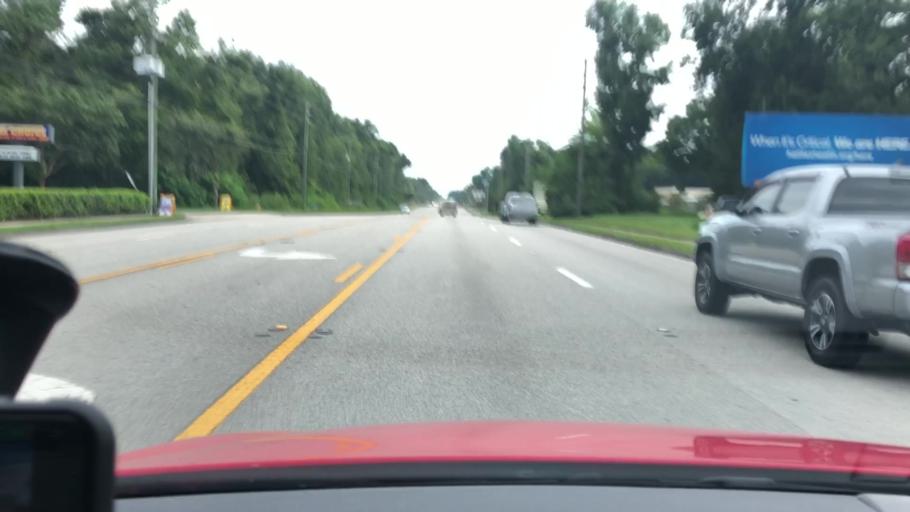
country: US
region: Florida
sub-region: Volusia County
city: DeLand
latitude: 29.0375
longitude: -81.3245
